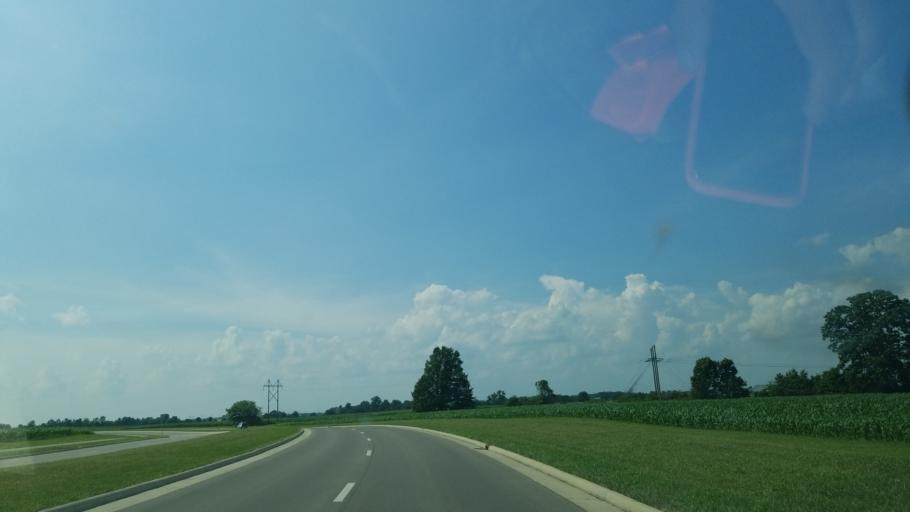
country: US
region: Ohio
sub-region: Delaware County
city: Delaware
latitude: 40.2653
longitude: -83.0916
